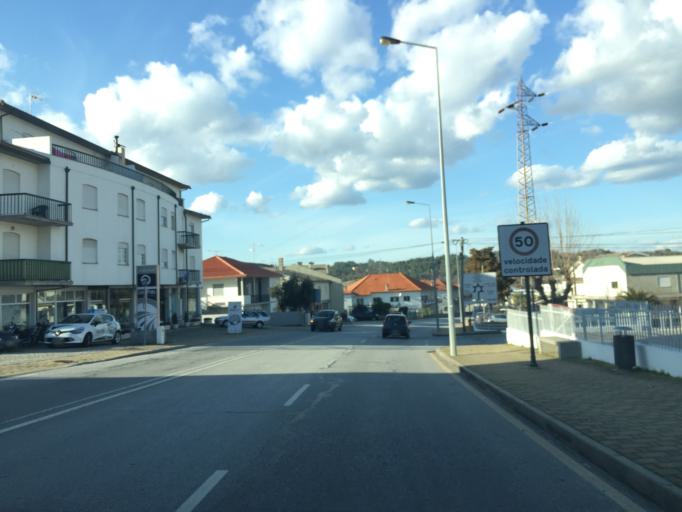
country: PT
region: Guarda
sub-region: Seia
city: Seia
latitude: 40.4244
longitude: -7.7145
